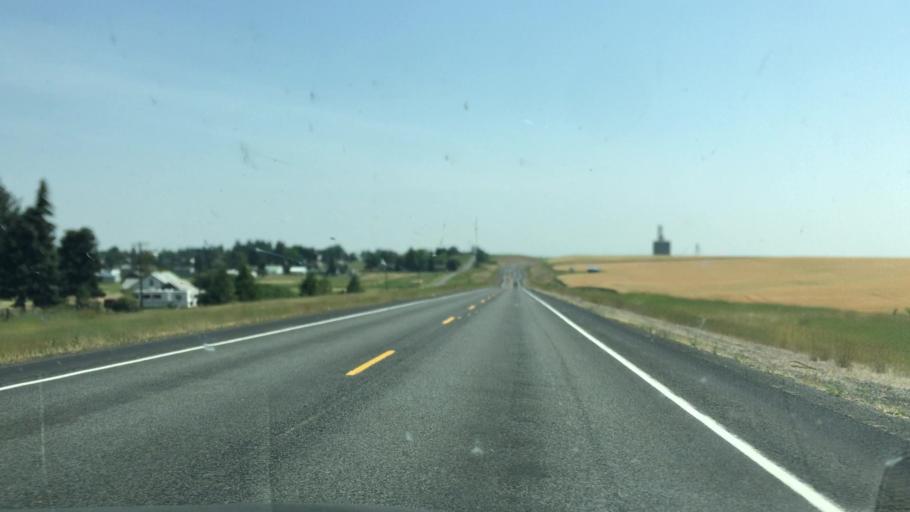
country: US
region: Idaho
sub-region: Lewis County
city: Nezperce
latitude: 46.2377
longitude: -116.4826
